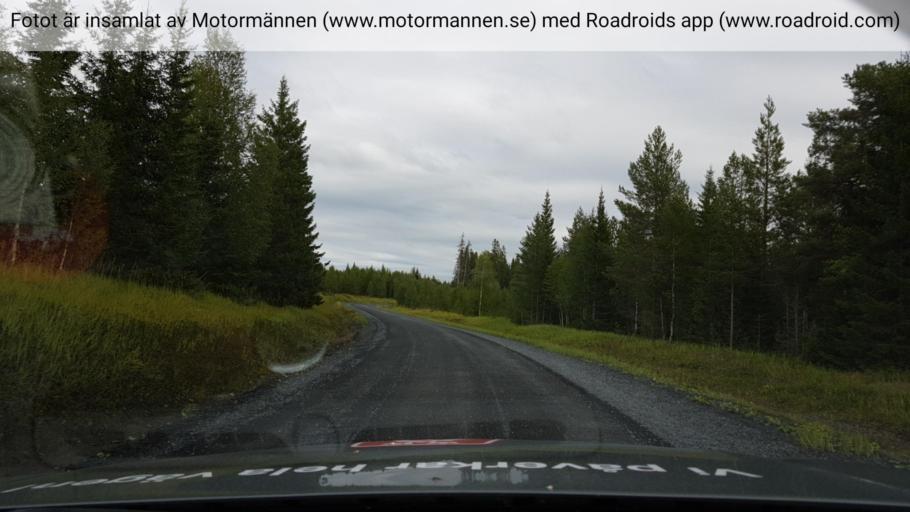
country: SE
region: Jaemtland
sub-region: Krokoms Kommun
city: Valla
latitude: 63.3660
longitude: 13.9226
